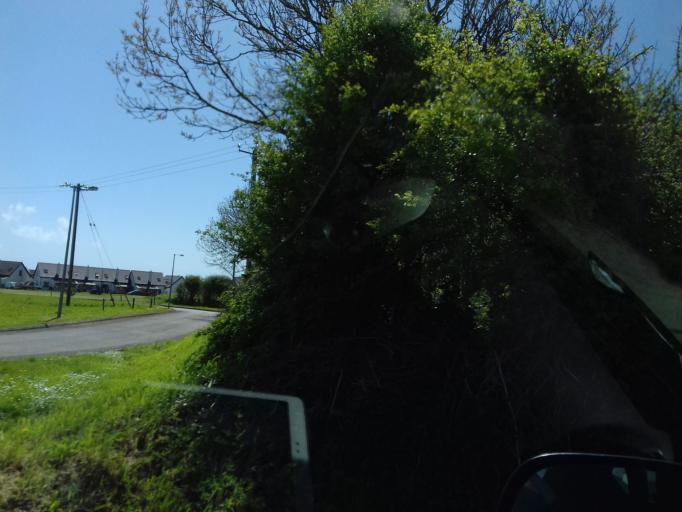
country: IE
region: Munster
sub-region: Waterford
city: Dunmore East
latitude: 52.1656
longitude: -6.8851
